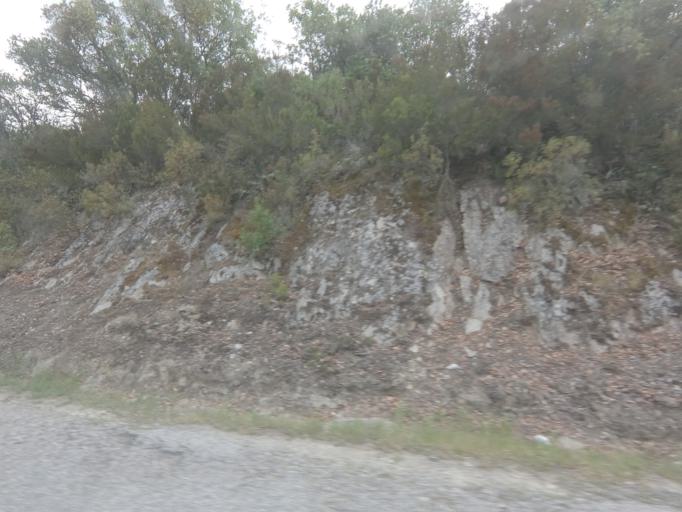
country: PT
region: Viseu
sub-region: Armamar
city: Armamar
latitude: 41.1256
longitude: -7.6557
